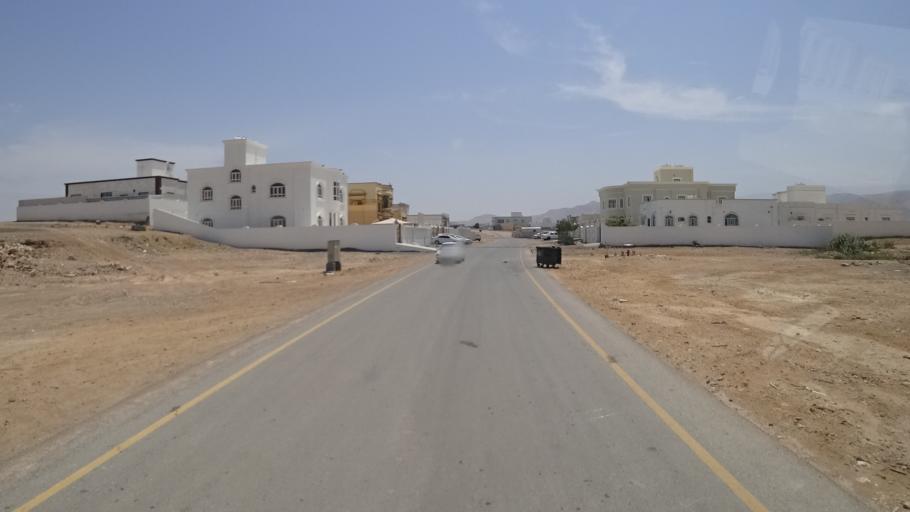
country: OM
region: Ash Sharqiyah
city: Sur
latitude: 22.6079
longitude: 59.4677
